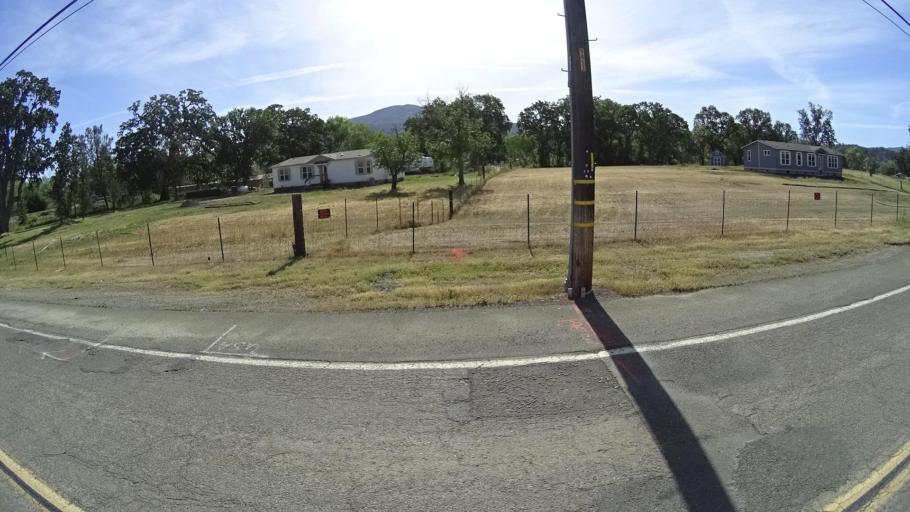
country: US
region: California
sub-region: Lake County
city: Kelseyville
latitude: 38.9733
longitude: -122.8388
